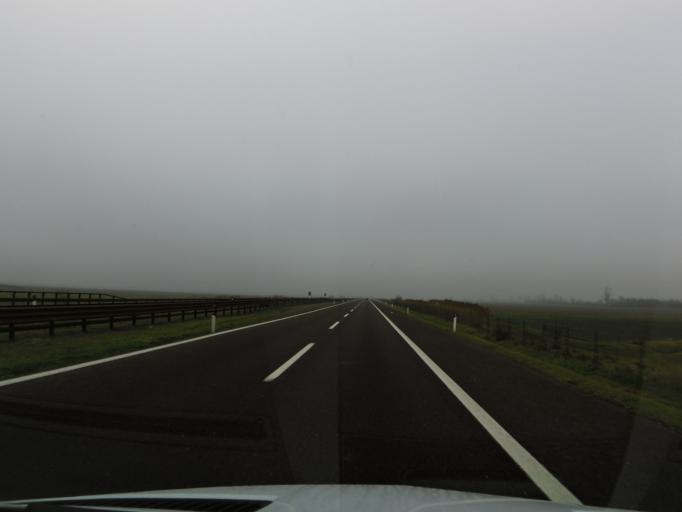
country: IT
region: Emilia-Romagna
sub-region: Provincia di Modena
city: Migliarina
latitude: 44.8408
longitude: 10.8524
